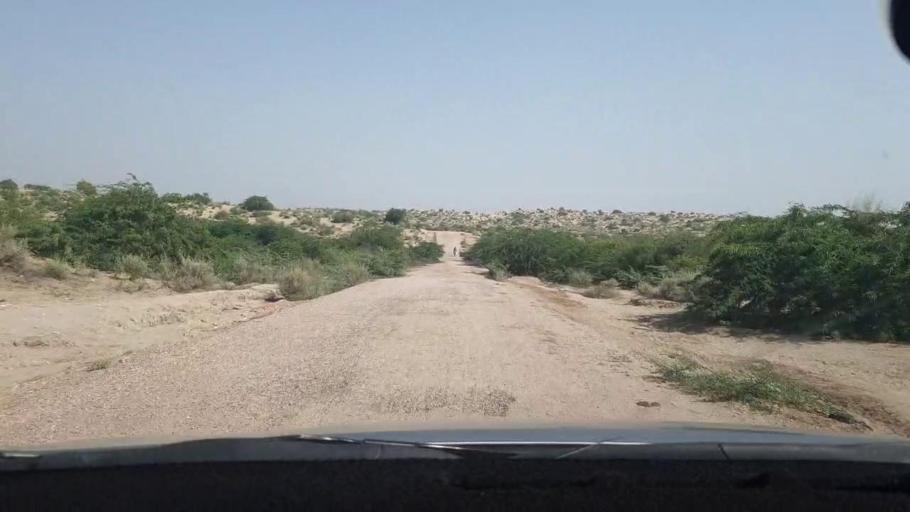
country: PK
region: Sindh
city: Pithoro
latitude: 25.7801
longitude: 69.4841
